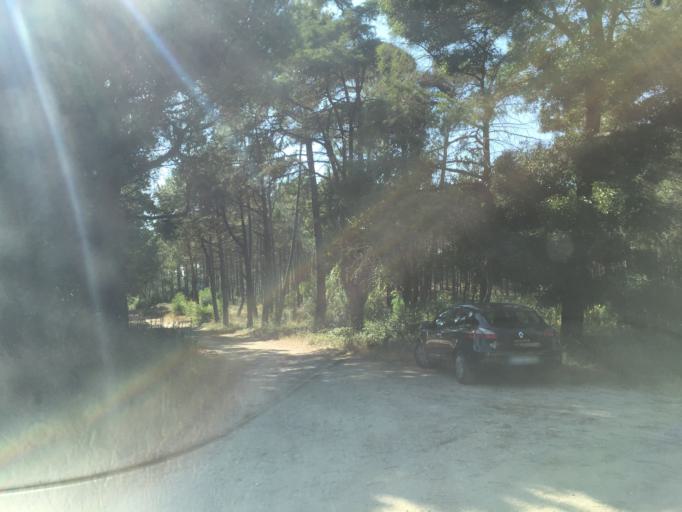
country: PT
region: Coimbra
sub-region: Figueira da Foz
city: Tavarede
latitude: 40.2273
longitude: -8.8486
